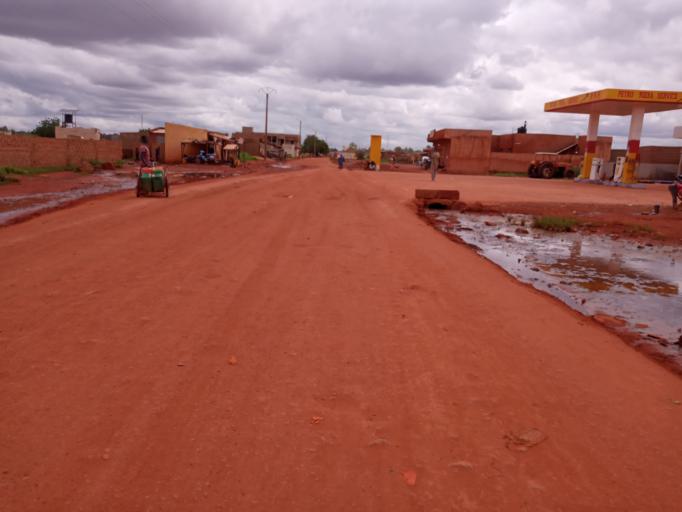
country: ML
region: Bamako
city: Bamako
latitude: 12.5400
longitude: -7.9944
